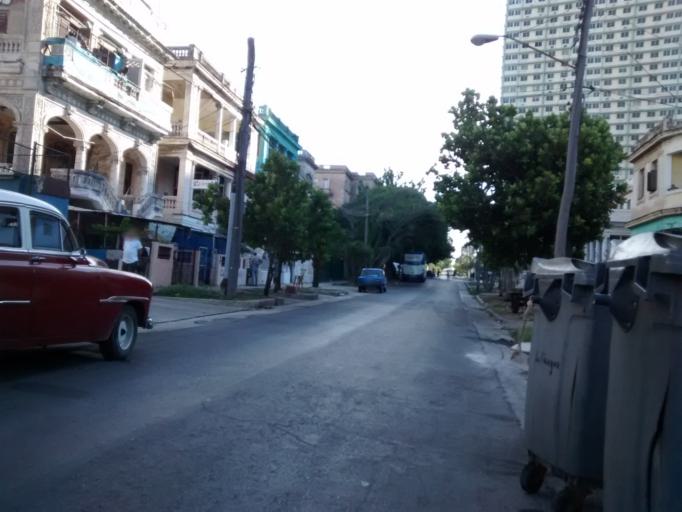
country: CU
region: La Habana
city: Havana
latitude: 23.1433
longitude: -82.3827
